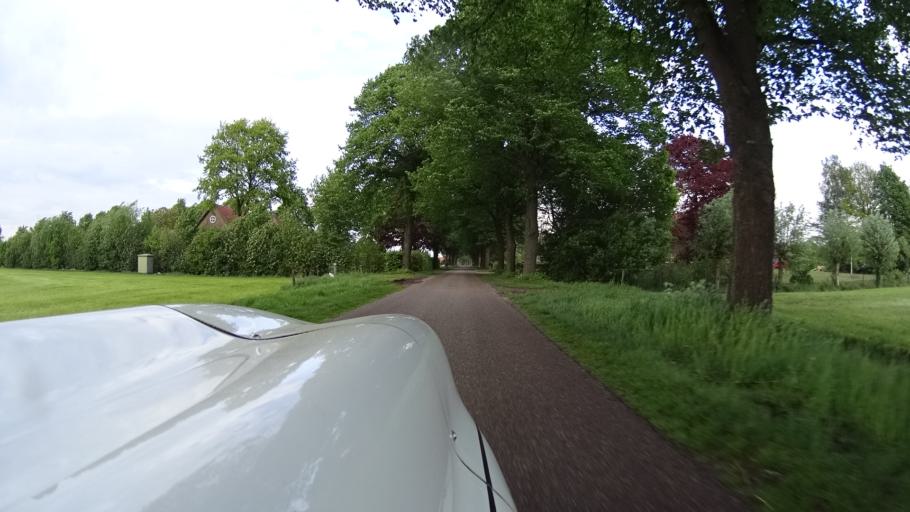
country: NL
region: North Brabant
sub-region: Gemeente Mill en Sint Hubert
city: Wilbertoord
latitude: 51.5948
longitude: 5.7918
